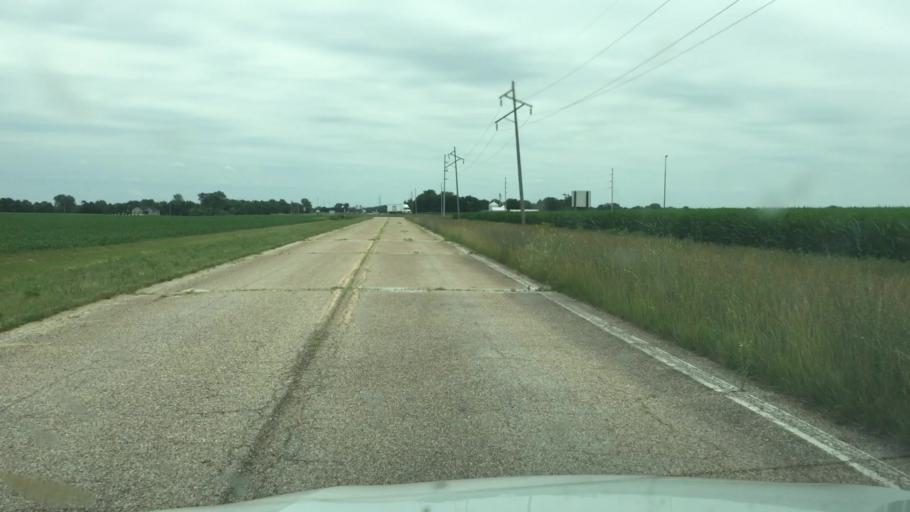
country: US
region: Illinois
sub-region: Hancock County
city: Carthage
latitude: 40.4159
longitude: -91.1106
